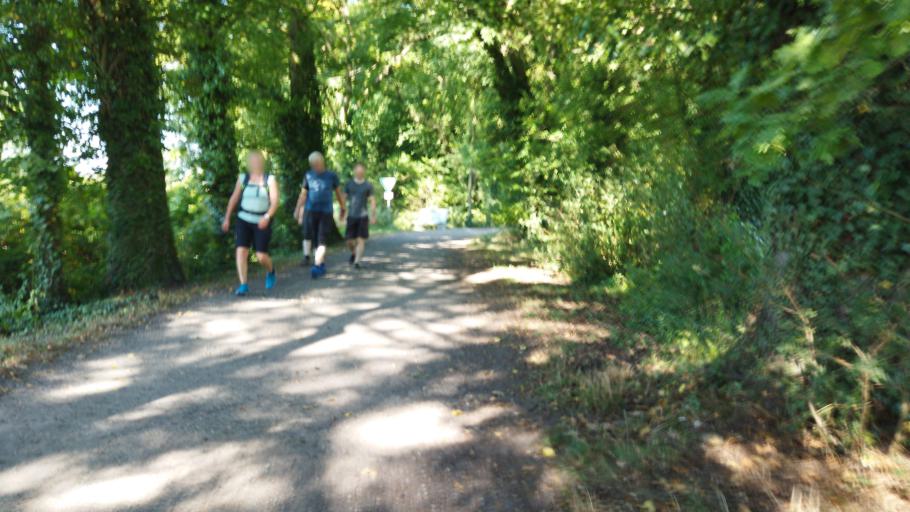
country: DE
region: North Rhine-Westphalia
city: Lengerich
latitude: 52.2002
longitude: 7.8356
